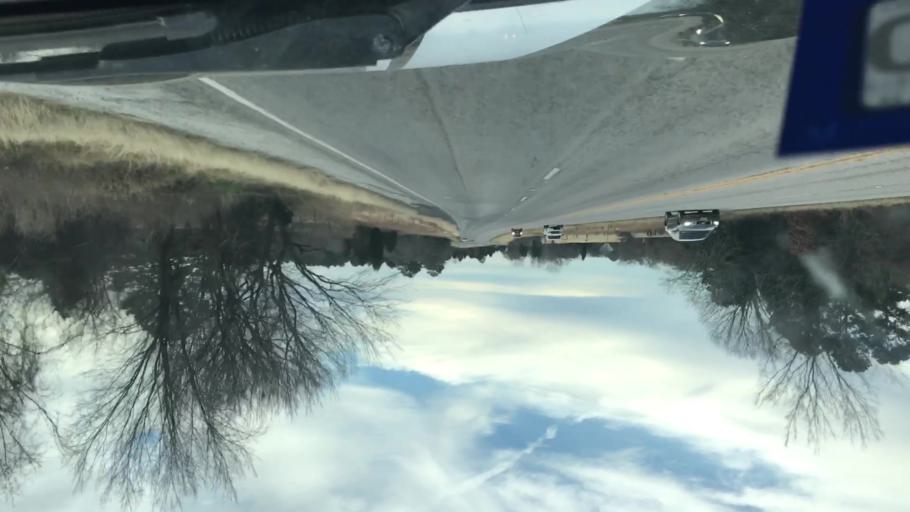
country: US
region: Texas
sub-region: Bastrop County
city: Elgin
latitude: 30.3012
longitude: -97.2912
